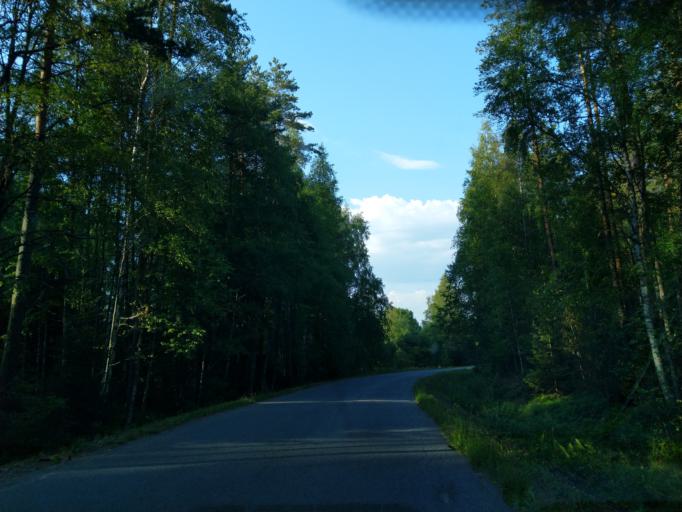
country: FI
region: Satakunta
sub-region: Pohjois-Satakunta
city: Honkajoki
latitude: 61.8142
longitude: 22.1938
